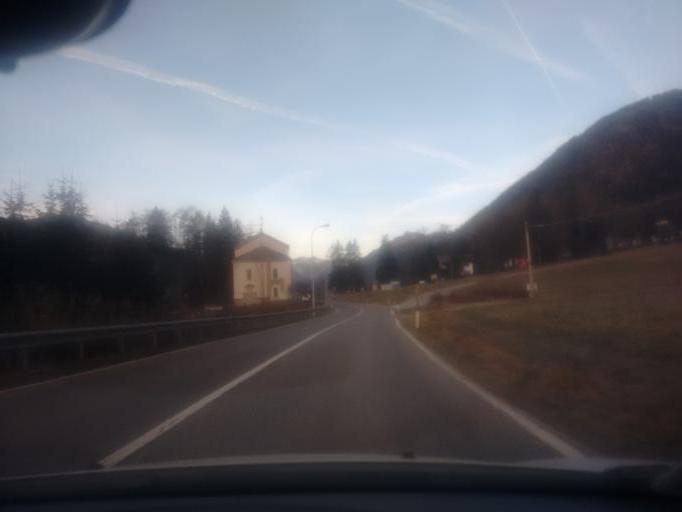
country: IT
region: Trentino-Alto Adige
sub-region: Bolzano
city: Campo di Trens
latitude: 46.8711
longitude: 11.4893
